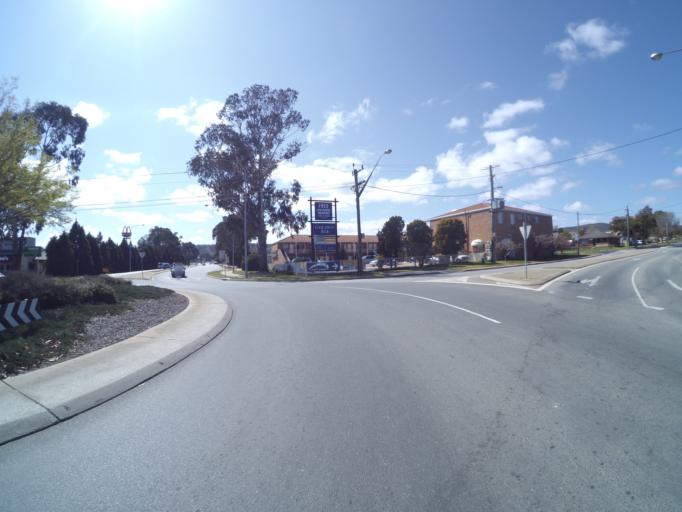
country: AU
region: New South Wales
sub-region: Queanbeyan
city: Queanbeyan
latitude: -35.3503
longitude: 149.2410
